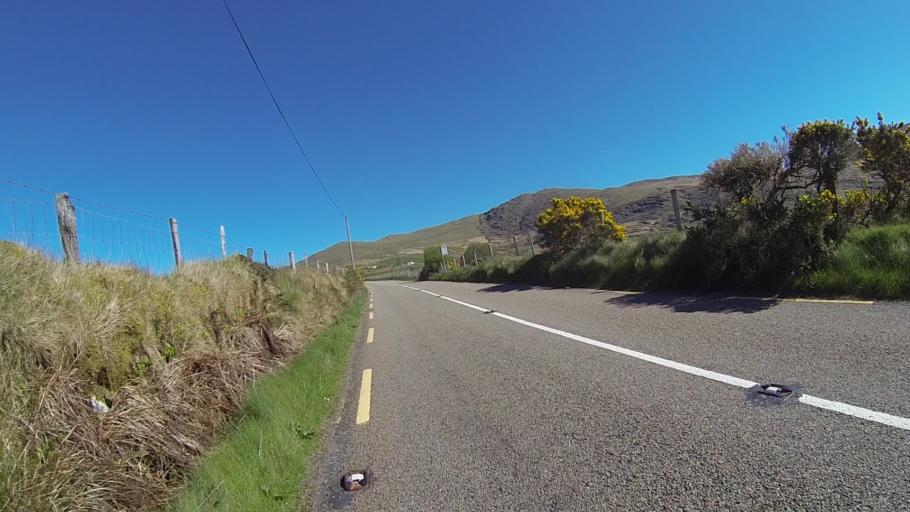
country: IE
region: Munster
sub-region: Ciarrai
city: Kenmare
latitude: 51.7780
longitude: -9.7297
